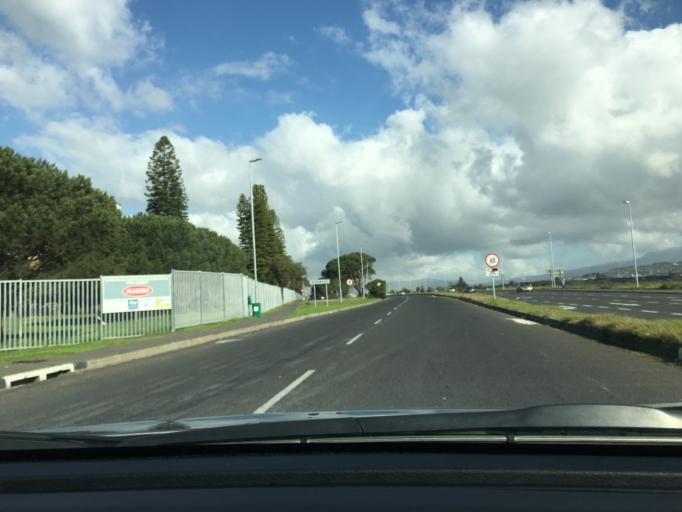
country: ZA
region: Western Cape
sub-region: City of Cape Town
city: Rosebank
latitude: -33.9523
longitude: 18.4863
